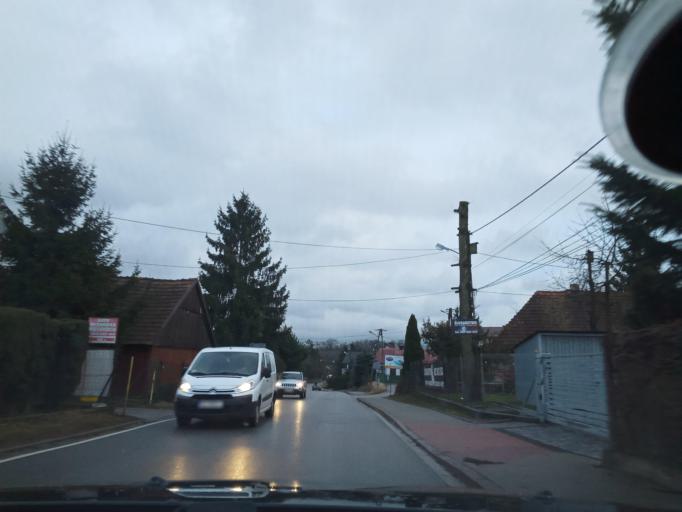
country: PL
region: Lesser Poland Voivodeship
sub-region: Powiat wielicki
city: Kokotow
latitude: 50.0092
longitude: 20.0845
